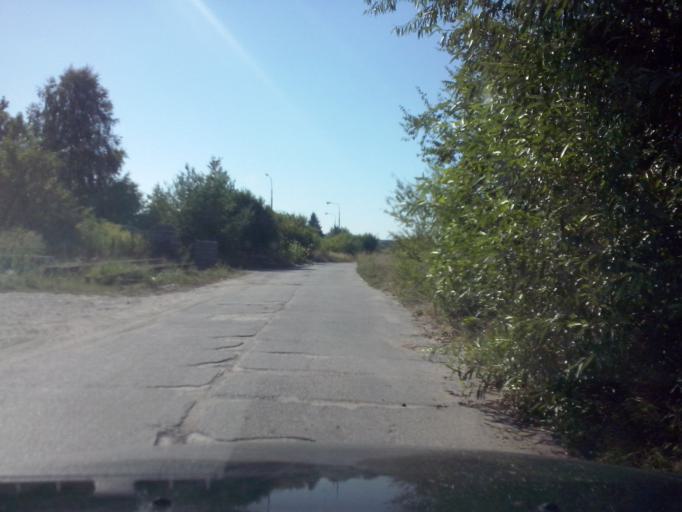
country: PL
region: Swietokrzyskie
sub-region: Powiat kielecki
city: Chmielnik
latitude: 50.6084
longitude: 20.7363
